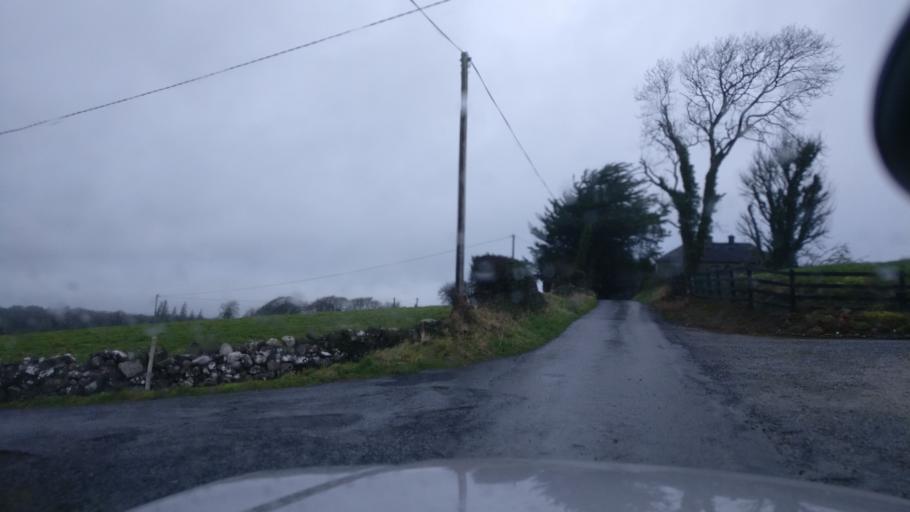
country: IE
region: Connaught
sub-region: County Galway
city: Loughrea
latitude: 53.1632
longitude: -8.6105
